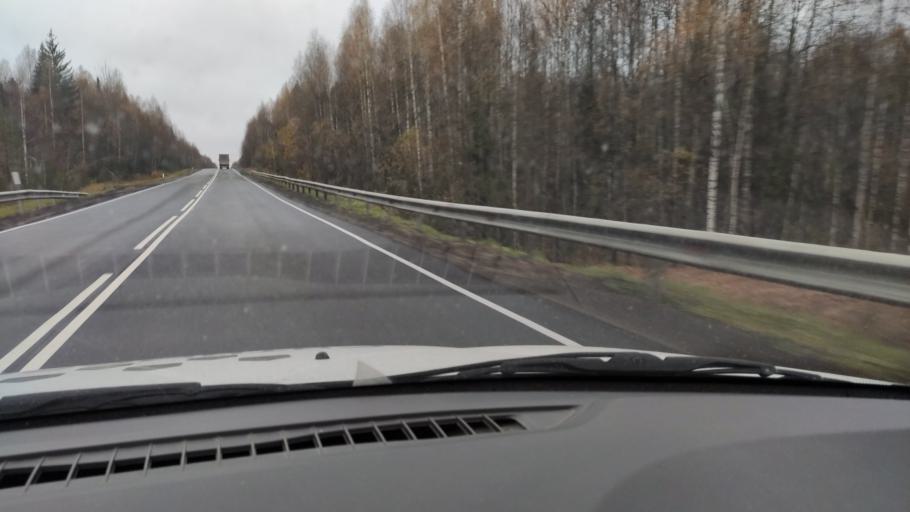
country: RU
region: Kirov
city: Omutninsk
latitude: 58.7635
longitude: 51.9955
